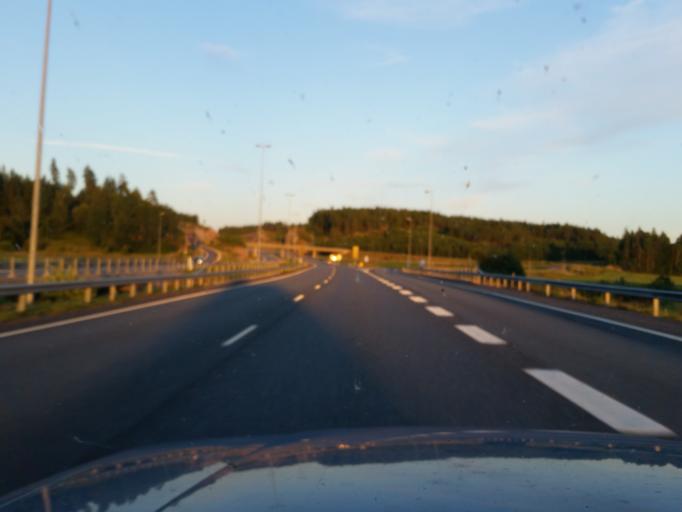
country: FI
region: Varsinais-Suomi
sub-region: Salo
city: Muurla
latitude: 60.3825
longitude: 23.3128
